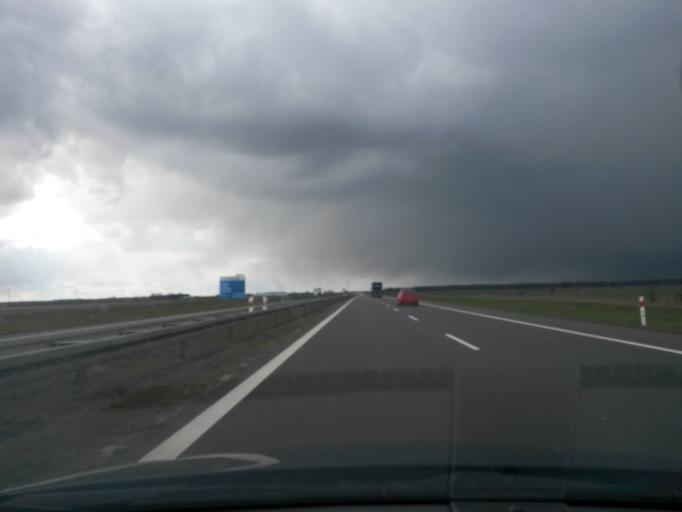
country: PL
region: Greater Poland Voivodeship
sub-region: Powiat sredzki
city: Dominowo
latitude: 52.3099
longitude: 17.3257
